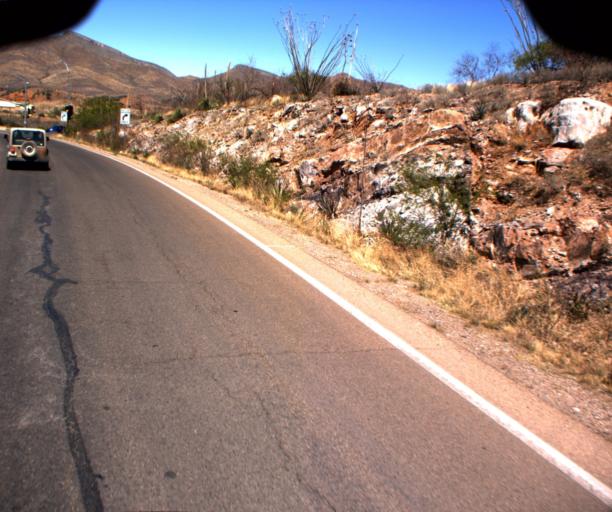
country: US
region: Arizona
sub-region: Cochise County
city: Bisbee
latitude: 31.4192
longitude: -109.8961
